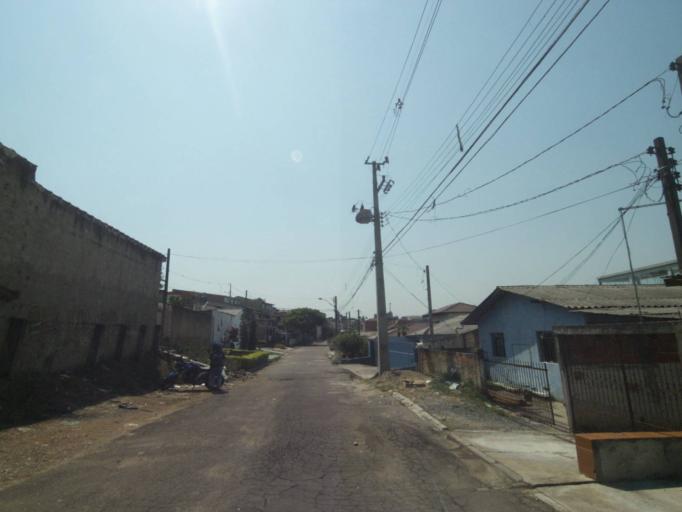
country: BR
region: Parana
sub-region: Sao Jose Dos Pinhais
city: Sao Jose dos Pinhais
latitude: -25.5099
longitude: -49.2725
